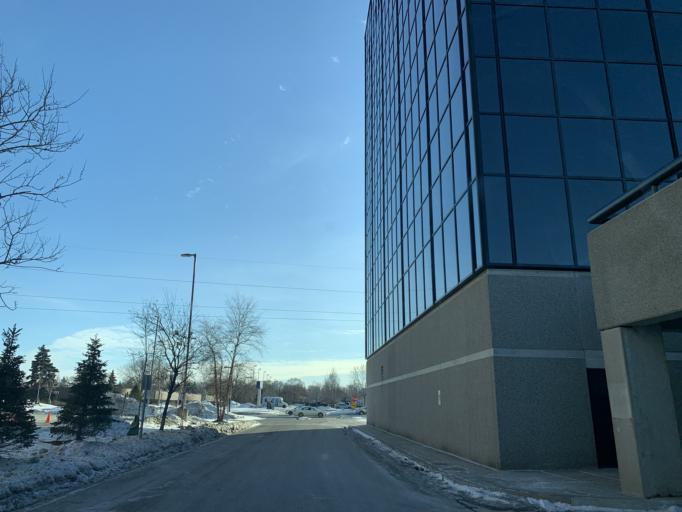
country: US
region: Minnesota
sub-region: Hennepin County
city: Richfield
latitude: 44.8608
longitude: -93.2518
